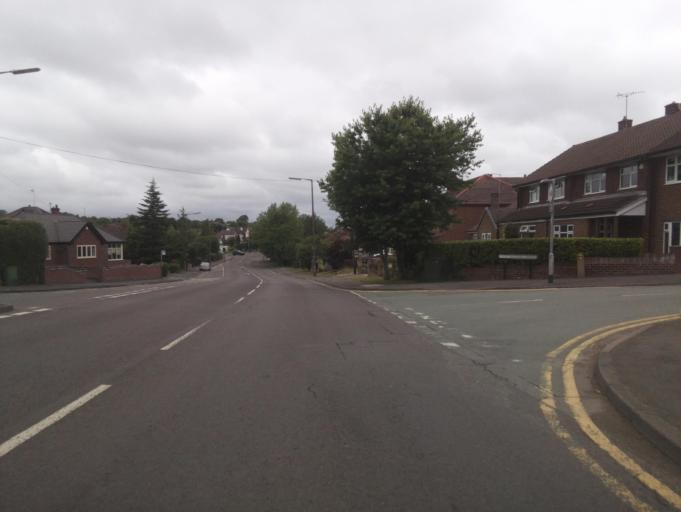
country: GB
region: England
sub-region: Staffordshire
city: Burton upon Trent
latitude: 52.8260
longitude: -1.6489
